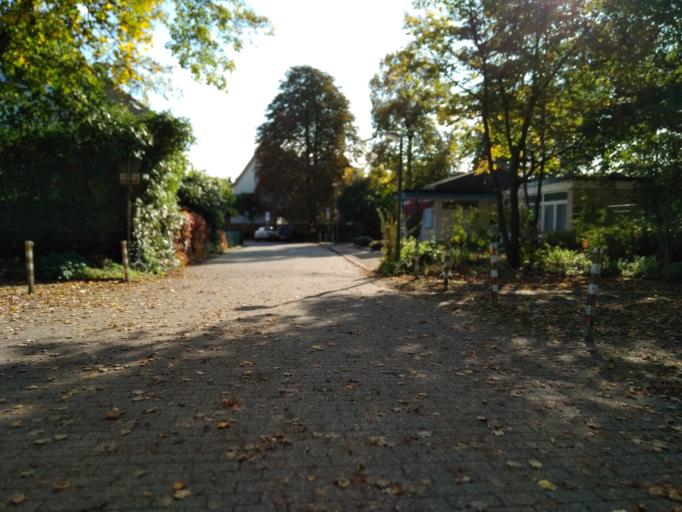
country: DE
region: North Rhine-Westphalia
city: Dorsten
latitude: 51.6629
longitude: 6.9621
